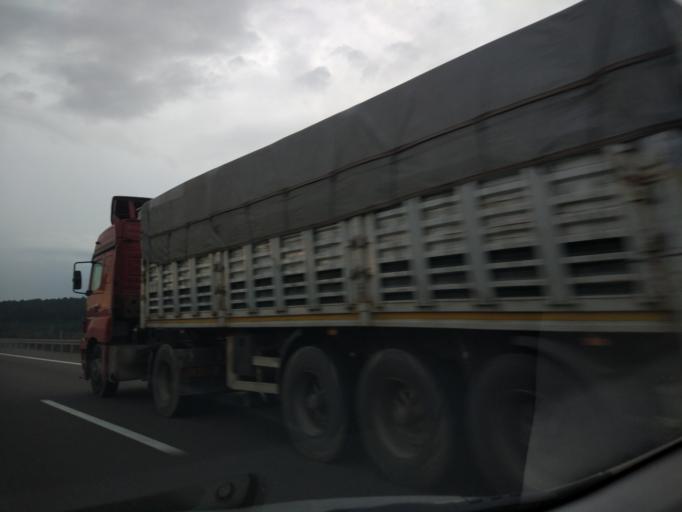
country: TR
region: Bolu
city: Yenicaga
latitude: 40.7542
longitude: 31.9205
